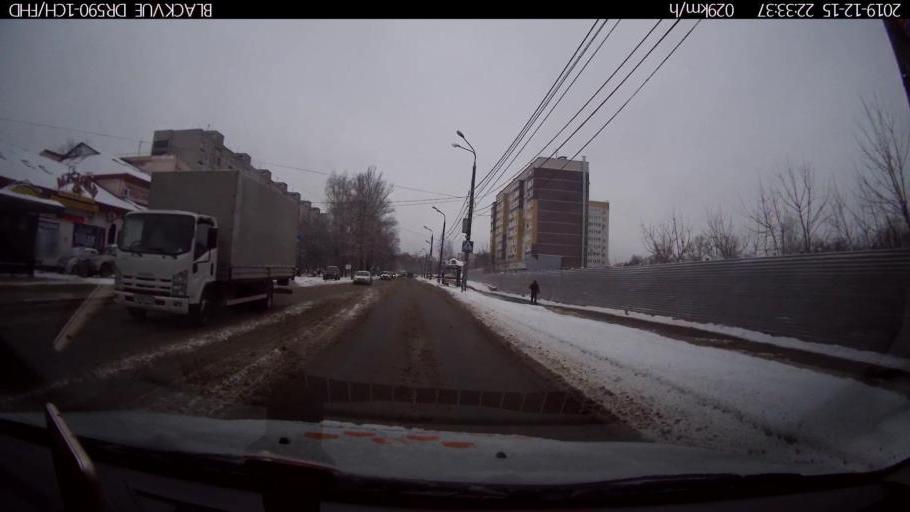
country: RU
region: Nizjnij Novgorod
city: Gorbatovka
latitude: 56.3427
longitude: 43.8333
